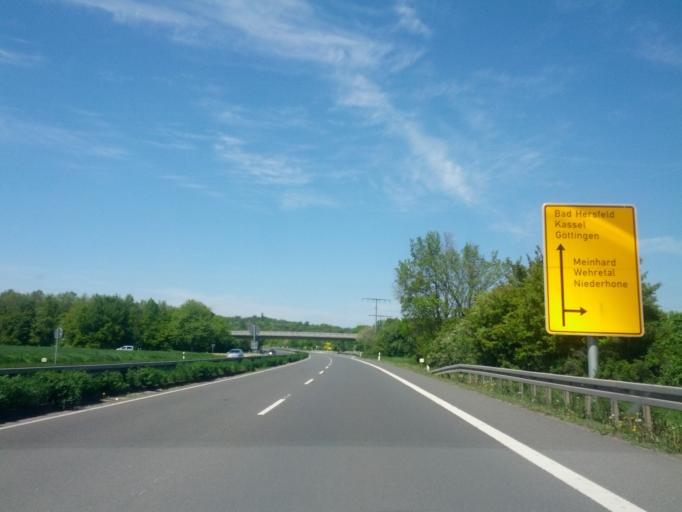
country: DE
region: Hesse
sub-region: Regierungsbezirk Kassel
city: Eschwege
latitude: 51.2012
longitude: 10.0126
